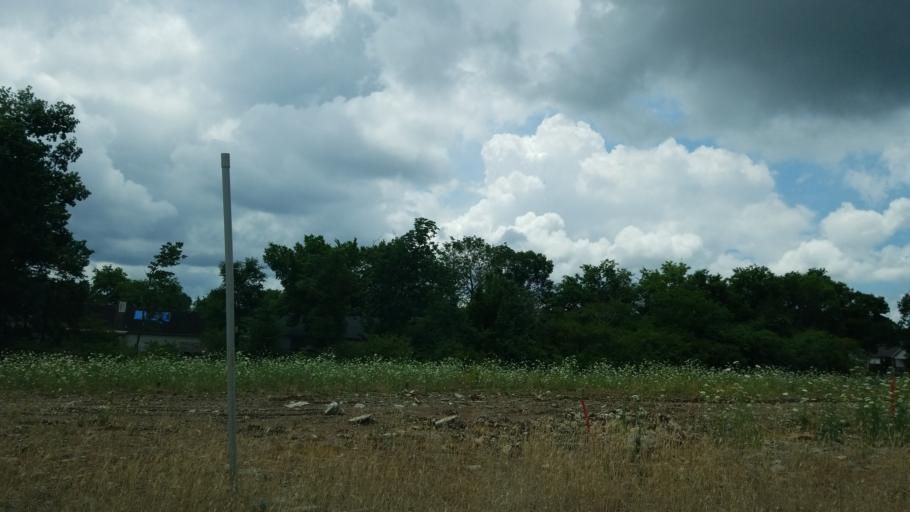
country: US
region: Tennessee
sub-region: Rutherford County
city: La Vergne
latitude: 36.0464
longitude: -86.5930
